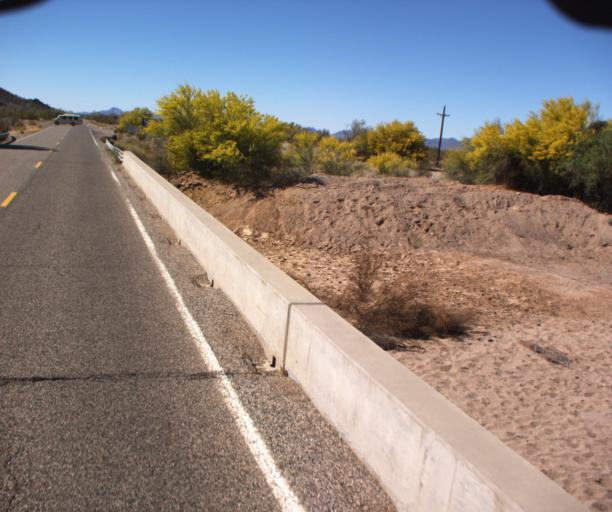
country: US
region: Arizona
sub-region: Pima County
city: Ajo
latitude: 32.2398
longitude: -112.7499
